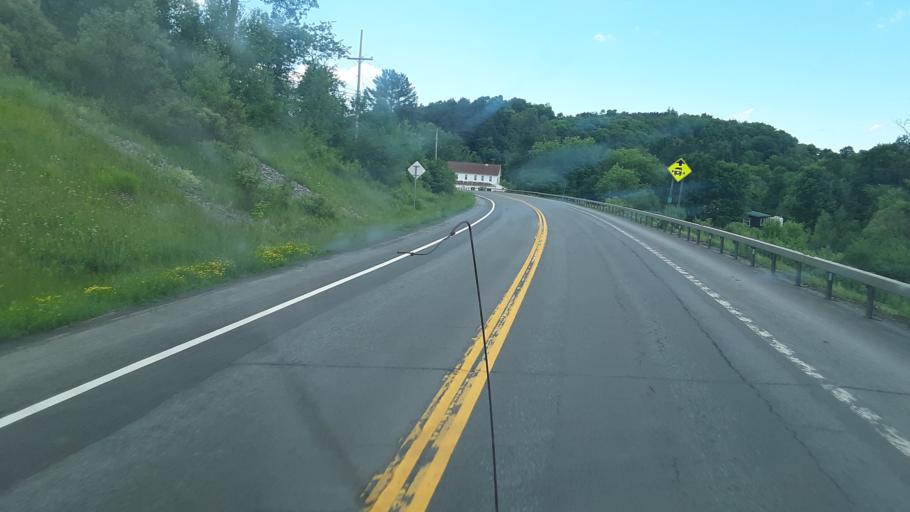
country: US
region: New York
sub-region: Oneida County
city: Rome
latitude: 43.3702
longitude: -75.4811
